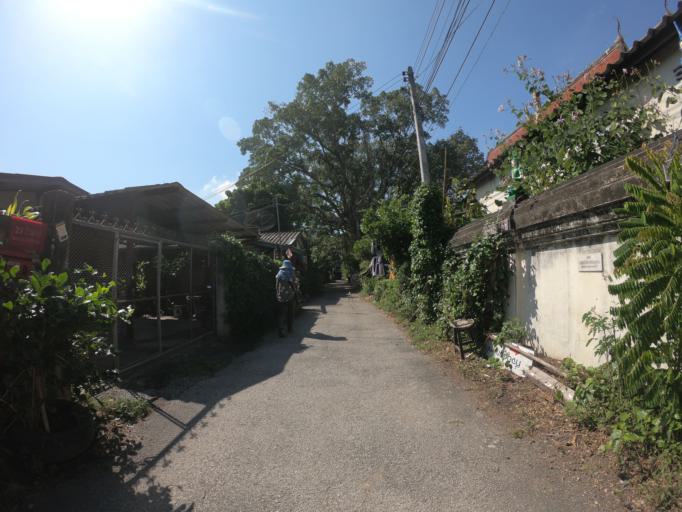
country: TH
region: Chiang Mai
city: Chiang Mai
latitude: 18.7766
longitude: 98.9851
